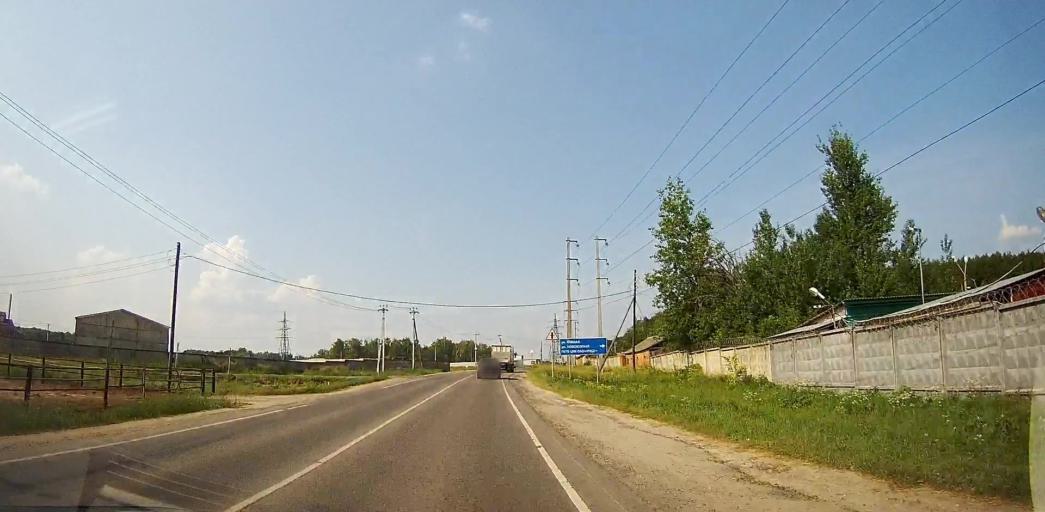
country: RU
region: Moskovskaya
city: Barybino
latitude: 55.2778
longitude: 37.9158
